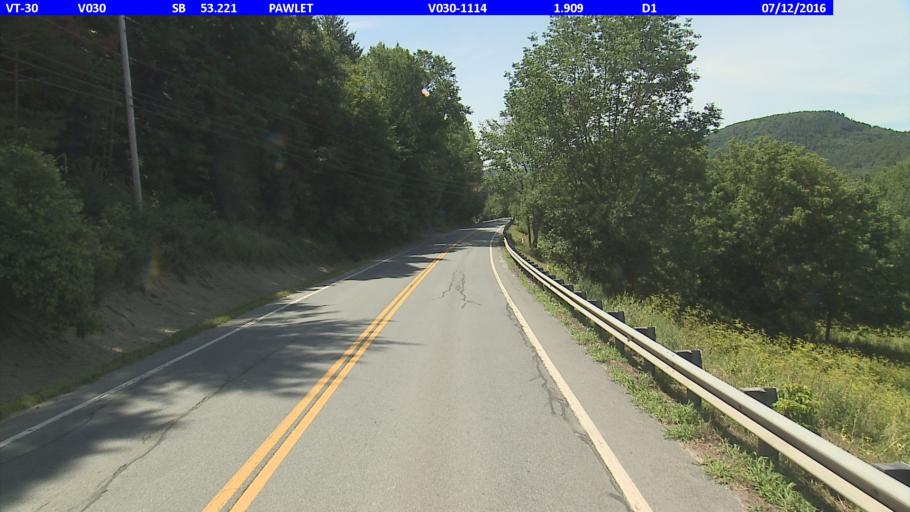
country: US
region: New York
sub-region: Washington County
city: Granville
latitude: 43.3376
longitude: -73.1767
